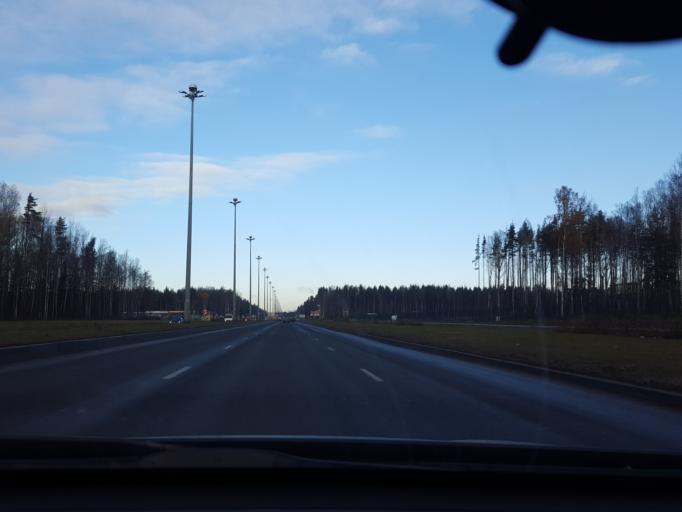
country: RU
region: Leningrad
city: Untolovo
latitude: 60.0490
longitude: 30.2316
